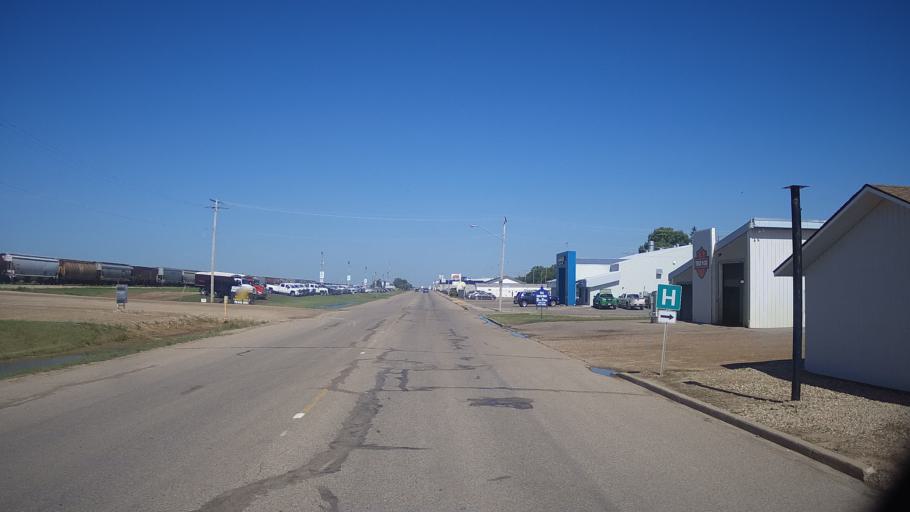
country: CA
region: Saskatchewan
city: Watrous
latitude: 51.6686
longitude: -105.4593
